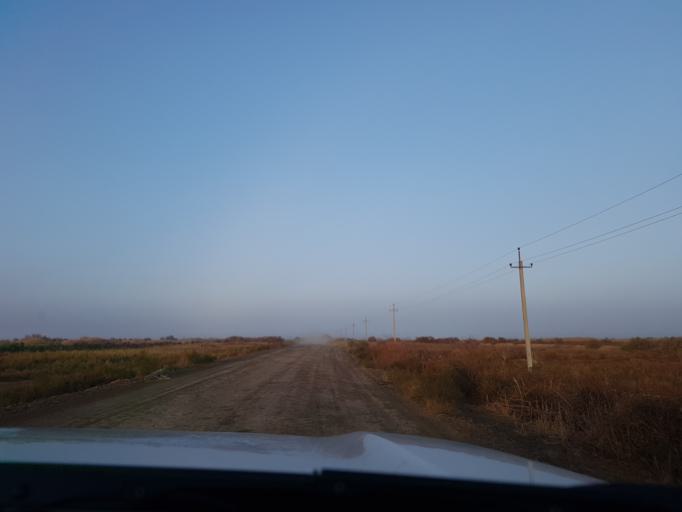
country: TM
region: Dasoguz
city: Koeneuergench
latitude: 41.8446
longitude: 58.5670
